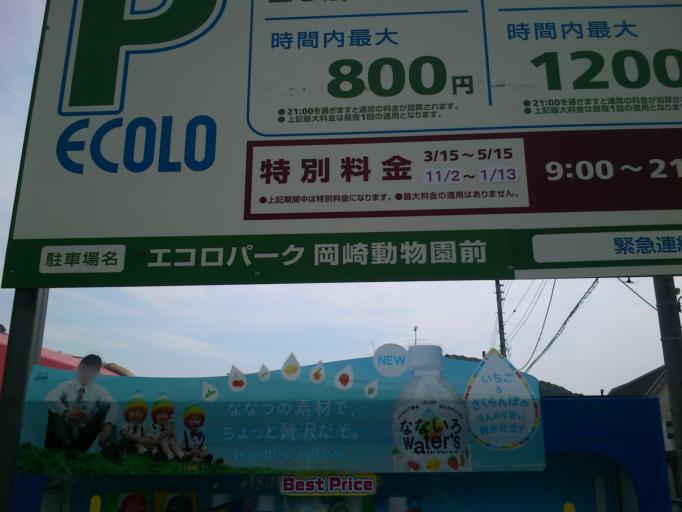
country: JP
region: Kyoto
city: Kyoto
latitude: 35.0136
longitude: 135.7880
